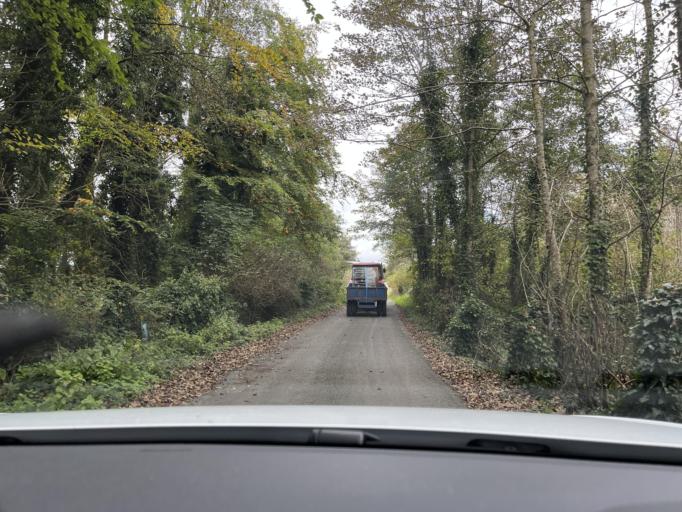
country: IE
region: Connaught
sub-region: Roscommon
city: Boyle
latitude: 53.9789
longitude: -8.2253
